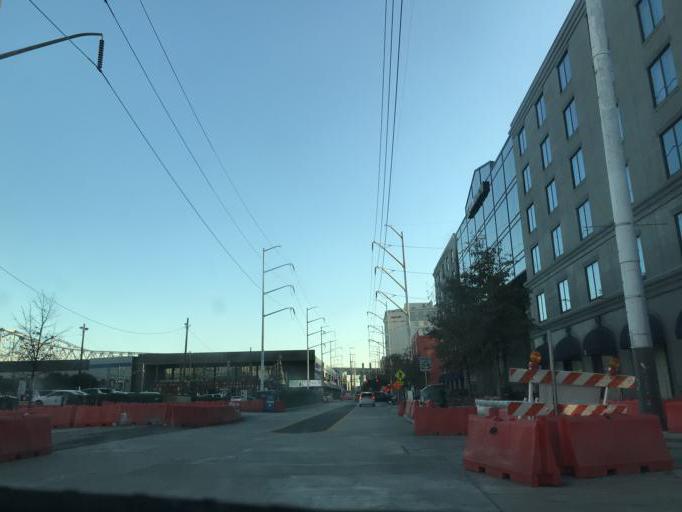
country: US
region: Louisiana
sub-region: Orleans Parish
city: New Orleans
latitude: 29.9460
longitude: -90.0648
